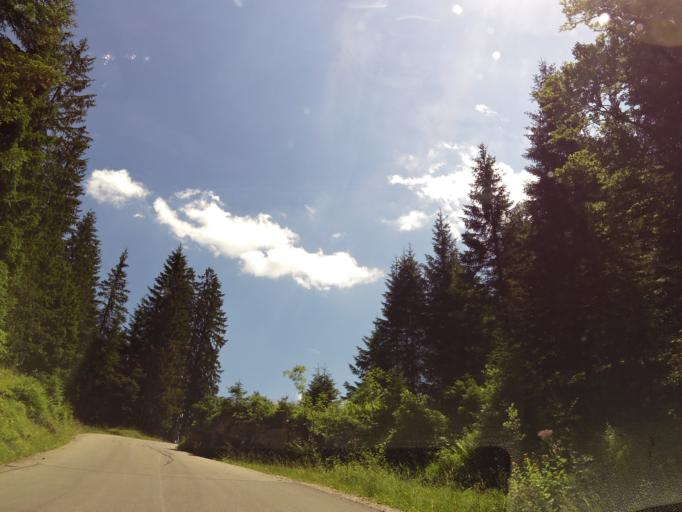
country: AT
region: Tyrol
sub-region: Politischer Bezirk Kitzbuhel
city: Waidring
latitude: 47.6590
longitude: 12.5753
